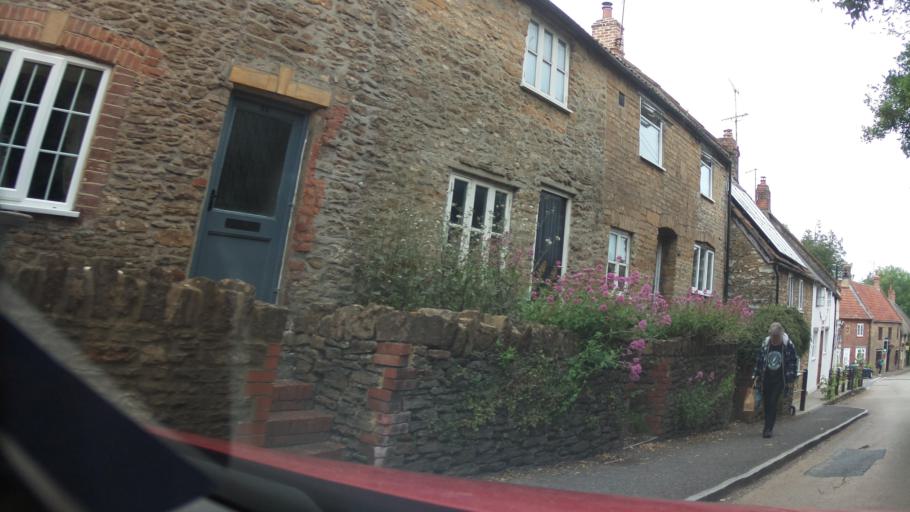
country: GB
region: England
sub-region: Somerset
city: Yeovil
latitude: 50.9189
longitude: -2.6877
